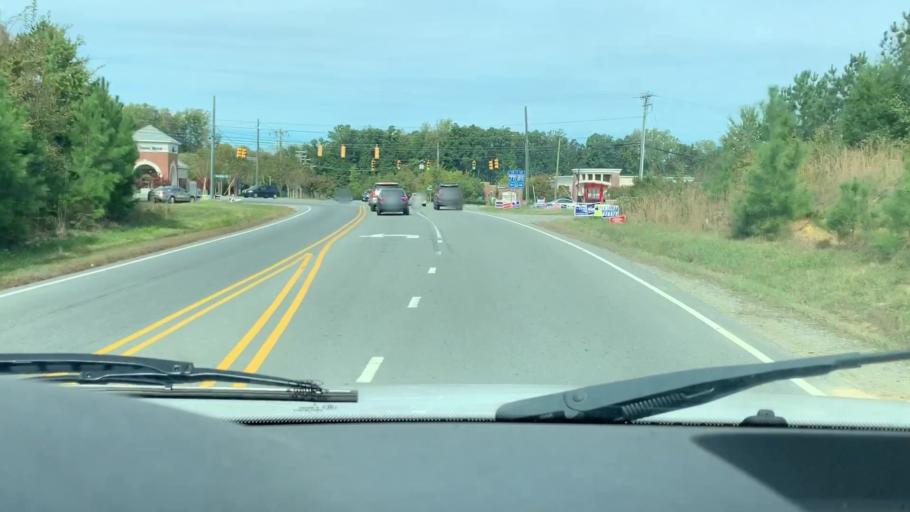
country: US
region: North Carolina
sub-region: Mecklenburg County
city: Huntersville
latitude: 35.4403
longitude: -80.7638
